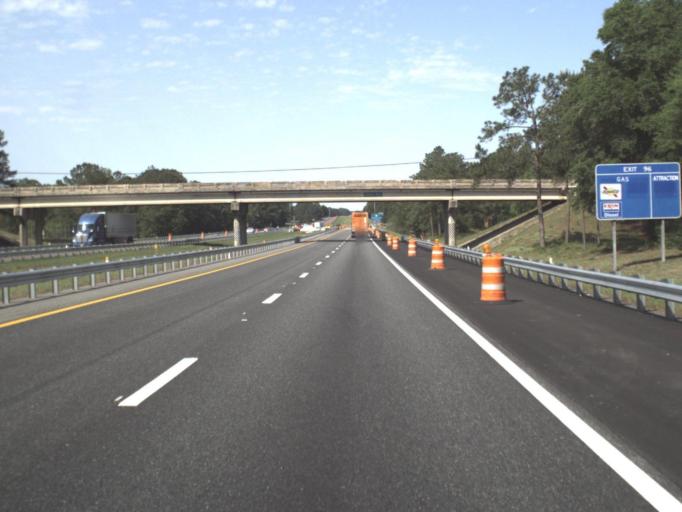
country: US
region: Florida
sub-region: Walton County
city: DeFuniak Springs
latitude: 30.7185
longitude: -85.9244
